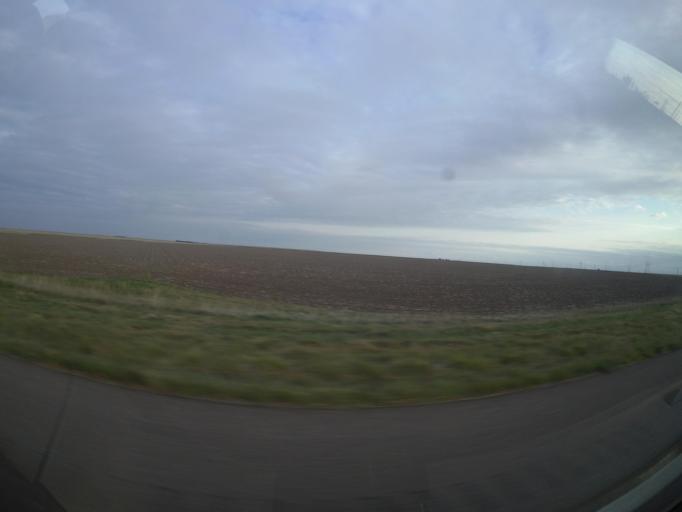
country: US
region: Colorado
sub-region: Yuma County
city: Wray
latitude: 39.7456
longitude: -102.2531
